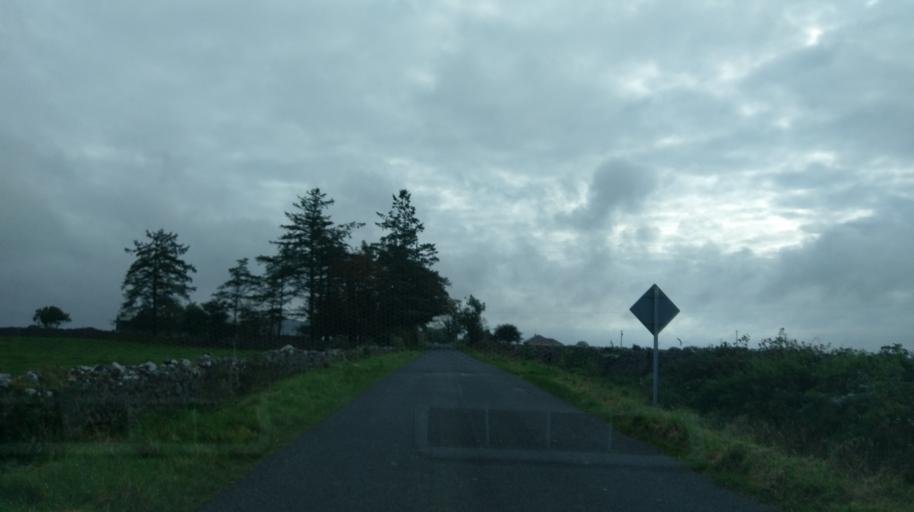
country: IE
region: Connaught
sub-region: County Galway
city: Athenry
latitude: 53.4632
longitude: -8.6300
